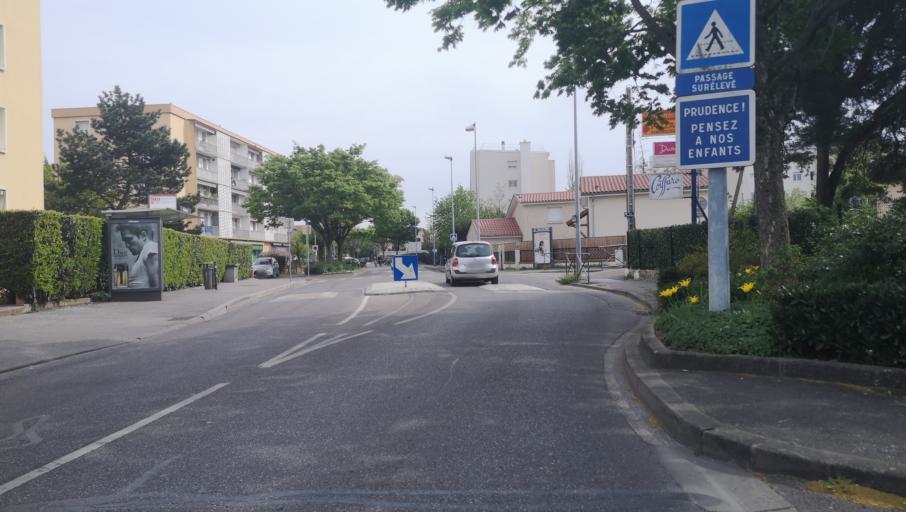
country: FR
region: Rhone-Alpes
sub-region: Departement du Rhone
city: Bron
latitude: 45.7409
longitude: 4.9201
